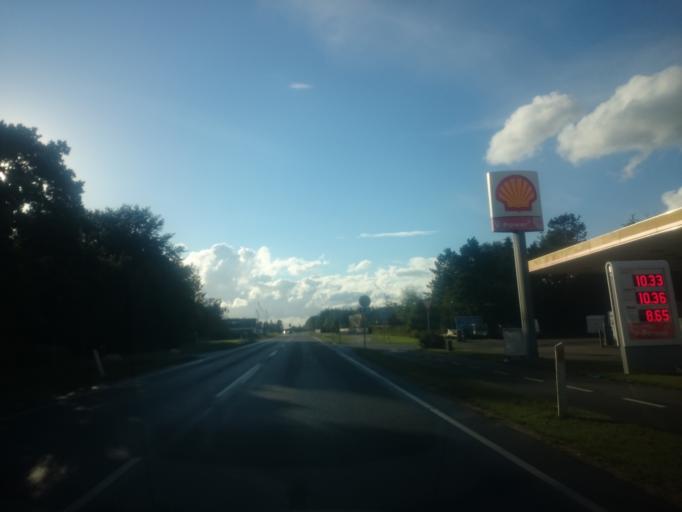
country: DK
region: South Denmark
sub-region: Billund Kommune
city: Billund
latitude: 55.7352
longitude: 9.1024
